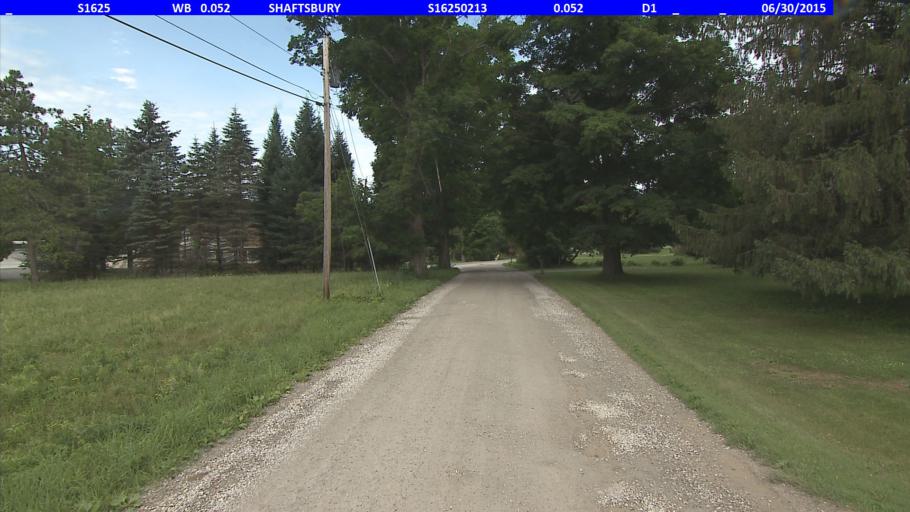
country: US
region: Vermont
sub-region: Bennington County
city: North Bennington
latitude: 42.9377
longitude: -73.2508
